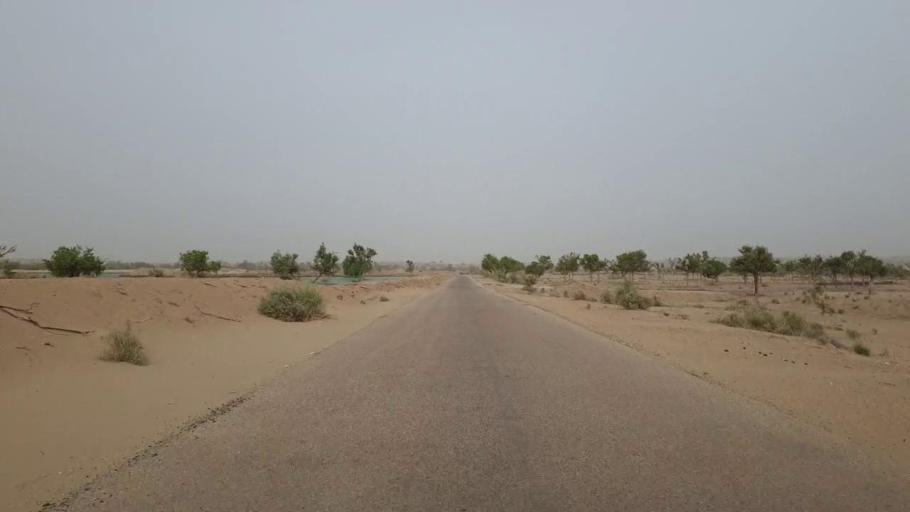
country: PK
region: Sindh
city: Islamkot
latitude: 24.5468
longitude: 70.3681
